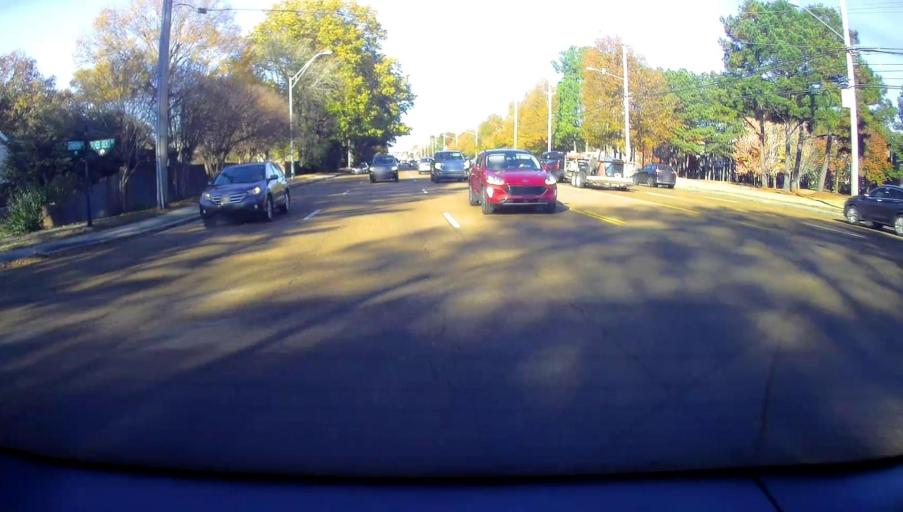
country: US
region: Tennessee
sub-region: Shelby County
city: Germantown
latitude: 35.1078
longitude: -89.8034
